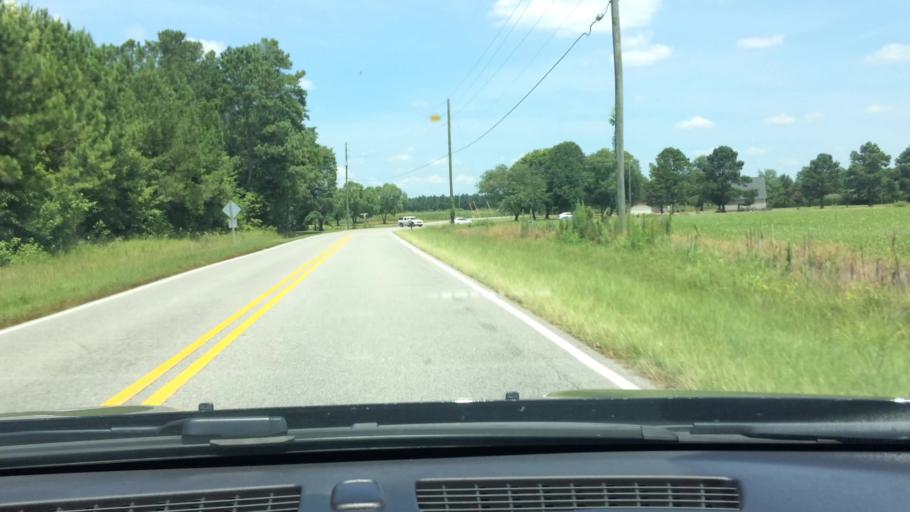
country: US
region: North Carolina
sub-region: Pitt County
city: Windsor
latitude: 35.5356
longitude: -77.3029
